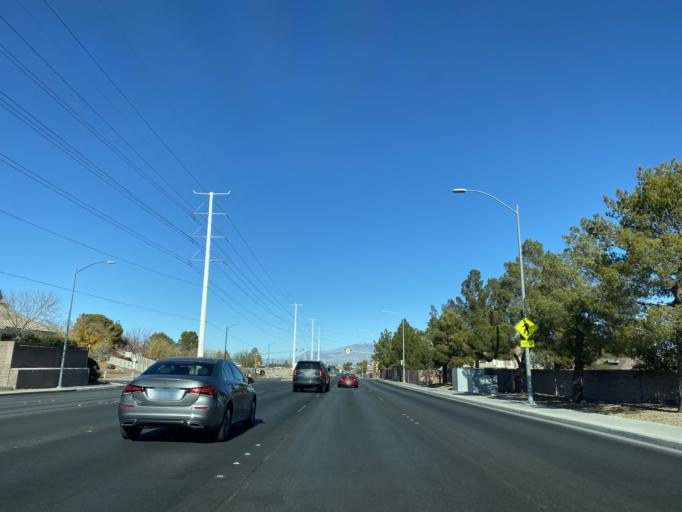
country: US
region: Nevada
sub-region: Clark County
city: Spring Valley
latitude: 36.1694
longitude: -115.2779
